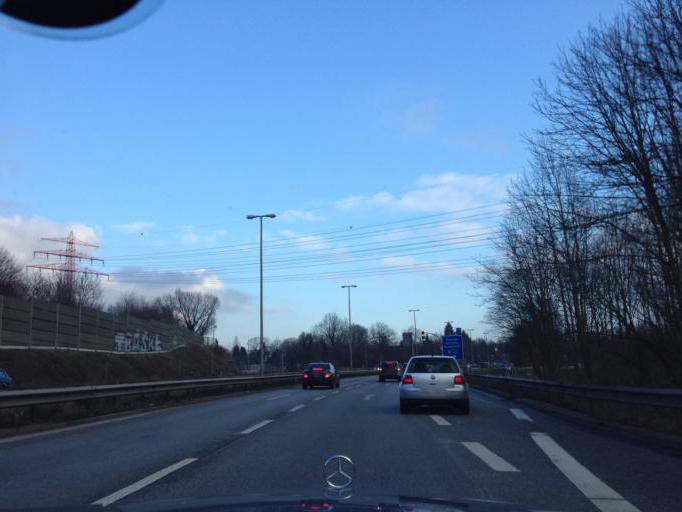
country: DE
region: Schleswig-Holstein
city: Oststeinbek
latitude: 53.5282
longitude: 10.1299
